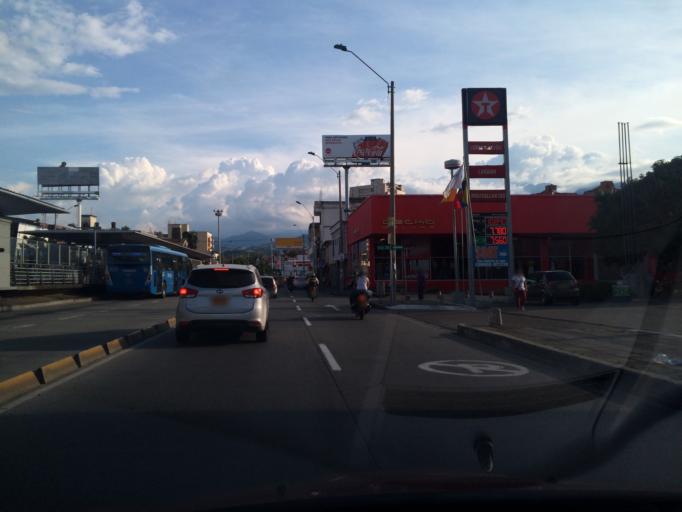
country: CO
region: Valle del Cauca
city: Cali
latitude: 3.4353
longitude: -76.5409
